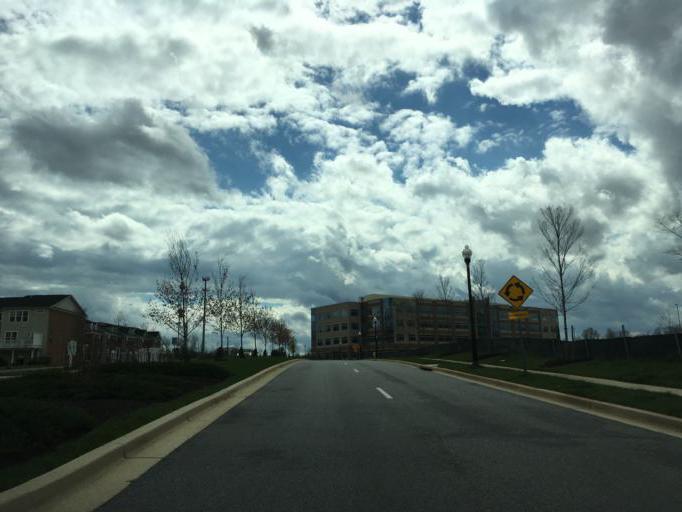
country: US
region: Maryland
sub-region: Anne Arundel County
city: Jessup
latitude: 39.1444
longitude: -76.7497
